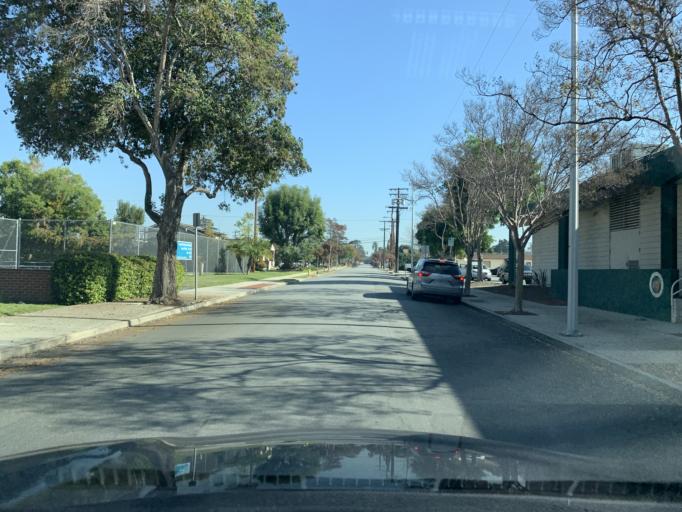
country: US
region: California
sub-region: Los Angeles County
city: Covina
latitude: 34.0885
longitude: -117.8875
